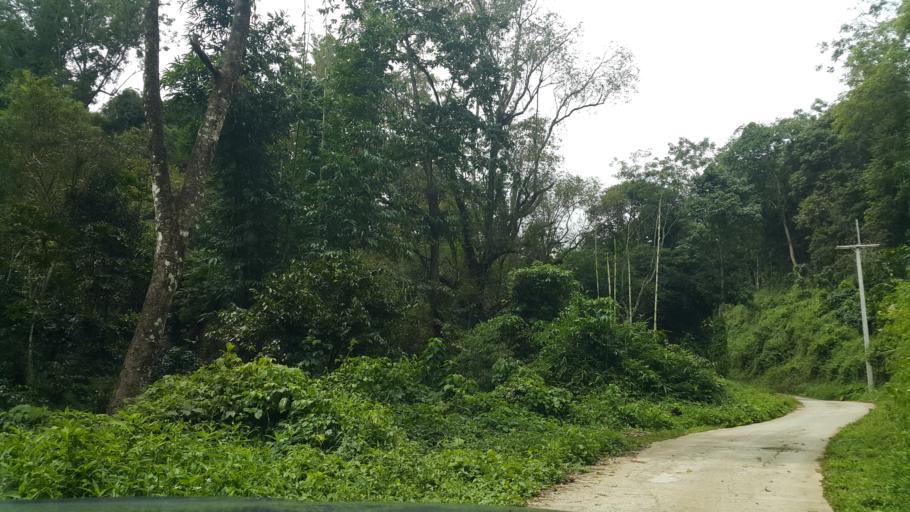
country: TH
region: Lampang
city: Wang Nuea
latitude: 19.0930
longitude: 99.3706
